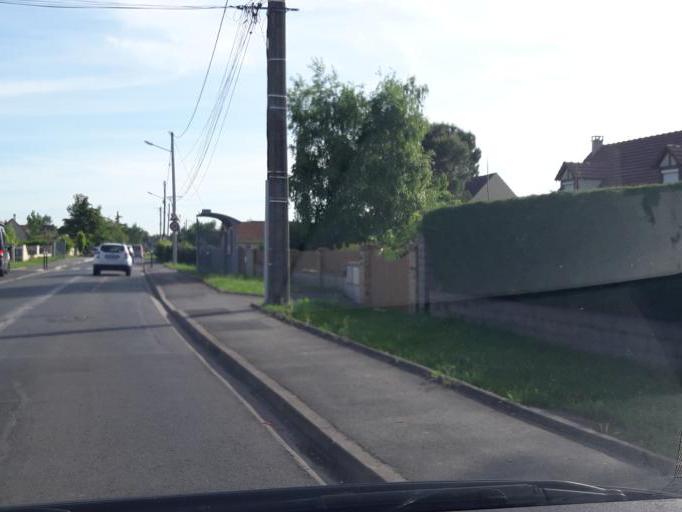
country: FR
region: Ile-de-France
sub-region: Departement de l'Essonne
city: Leudeville
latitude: 48.5601
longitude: 2.3188
